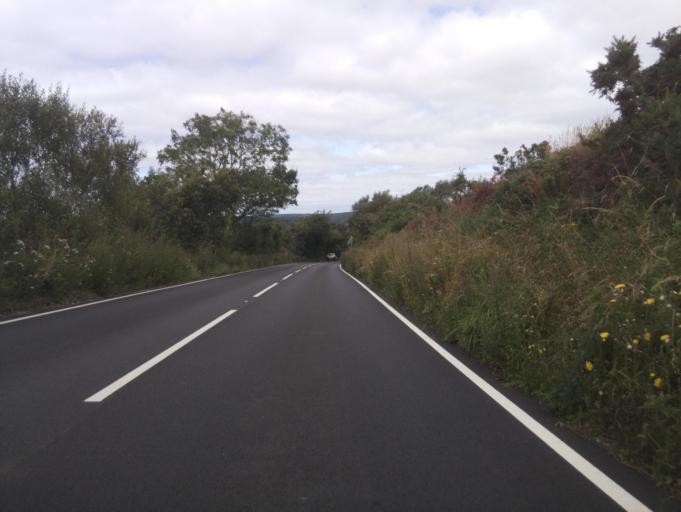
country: GB
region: England
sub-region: Devon
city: Bishopsteignton
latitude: 50.5825
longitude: -3.5322
